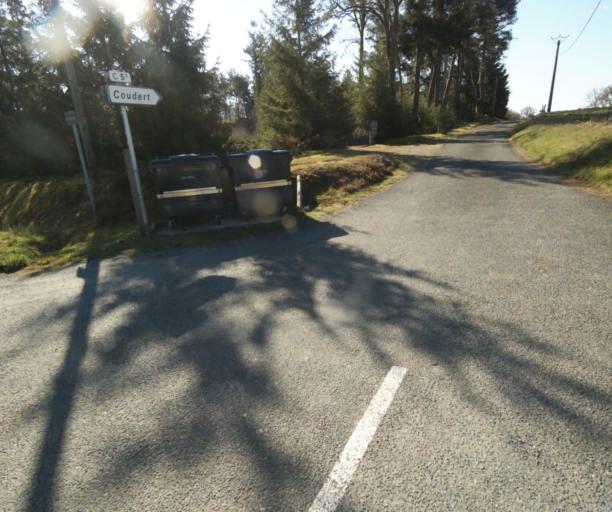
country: FR
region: Limousin
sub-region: Departement de la Correze
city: Correze
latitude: 45.2799
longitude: 1.9431
